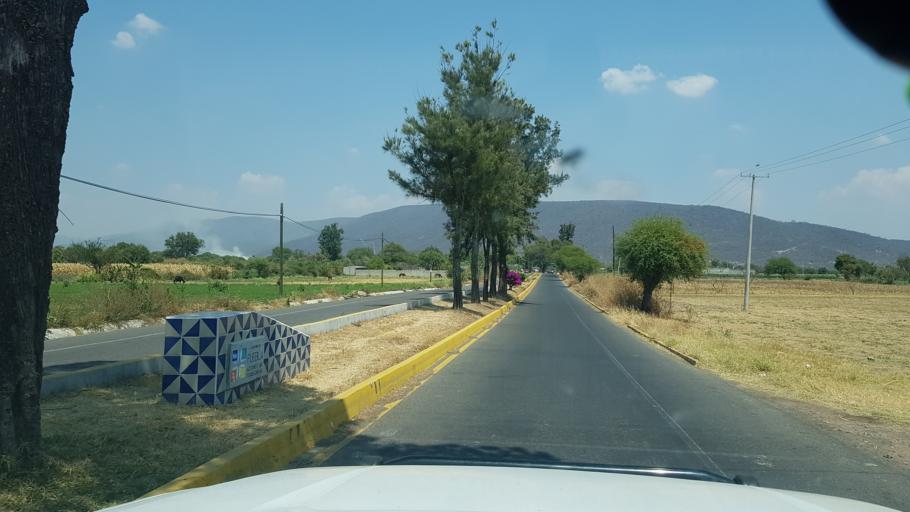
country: MX
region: Puebla
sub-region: Huaquechula
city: Cacaloxuchitl
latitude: 18.7902
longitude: -98.4594
